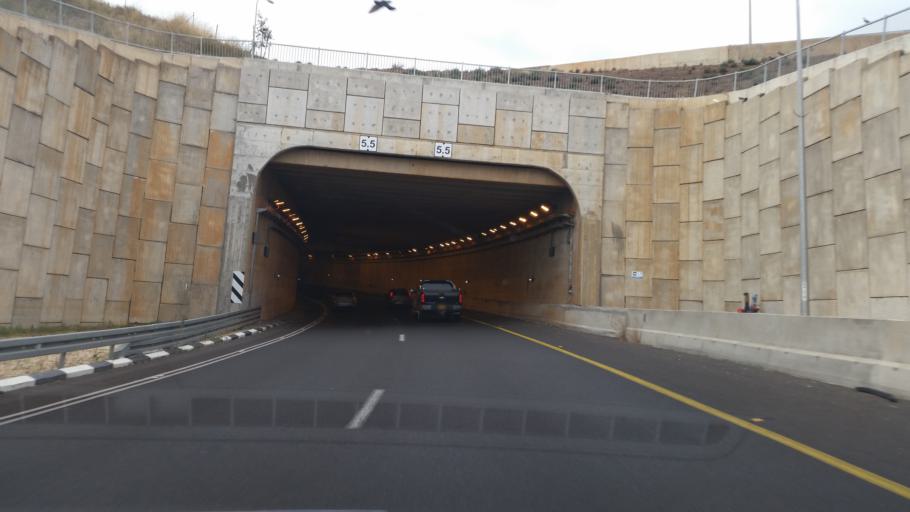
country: IL
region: Tel Aviv
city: Kefar Shemaryahu
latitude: 32.1945
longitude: 34.8314
